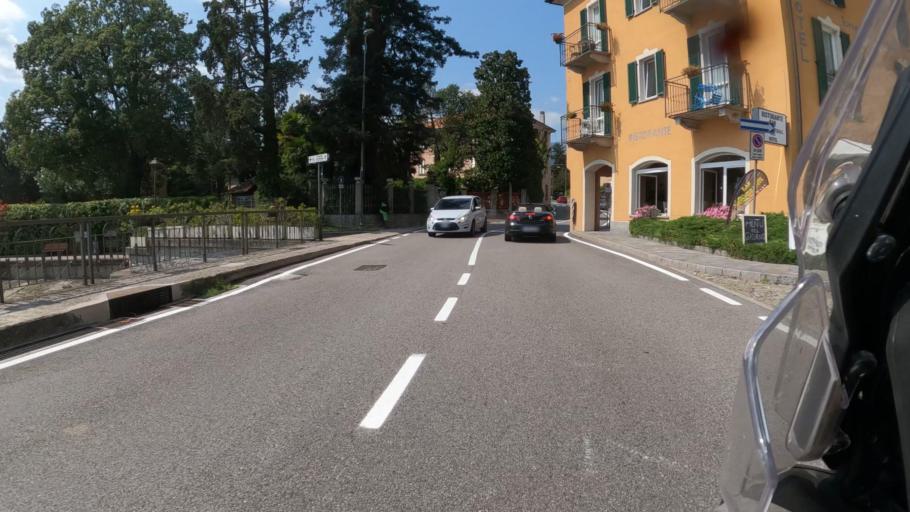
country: IT
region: Lombardy
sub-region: Provincia di Varese
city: Maccagno
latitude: 46.0363
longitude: 8.7425
